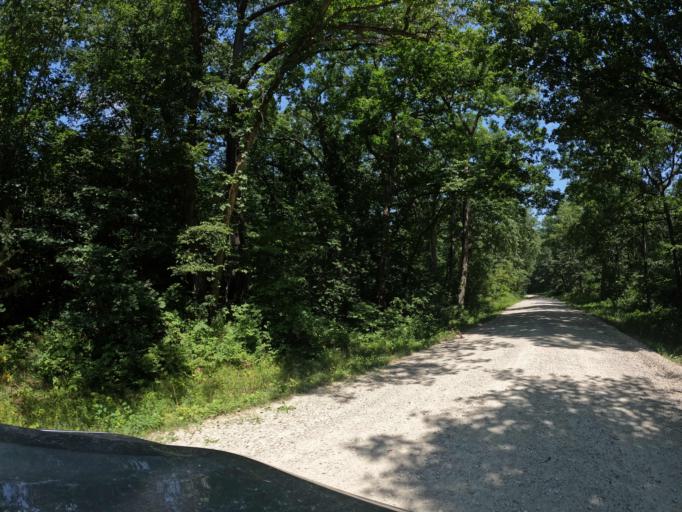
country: US
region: Iowa
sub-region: Henry County
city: Mount Pleasant
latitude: 40.8906
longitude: -91.6882
